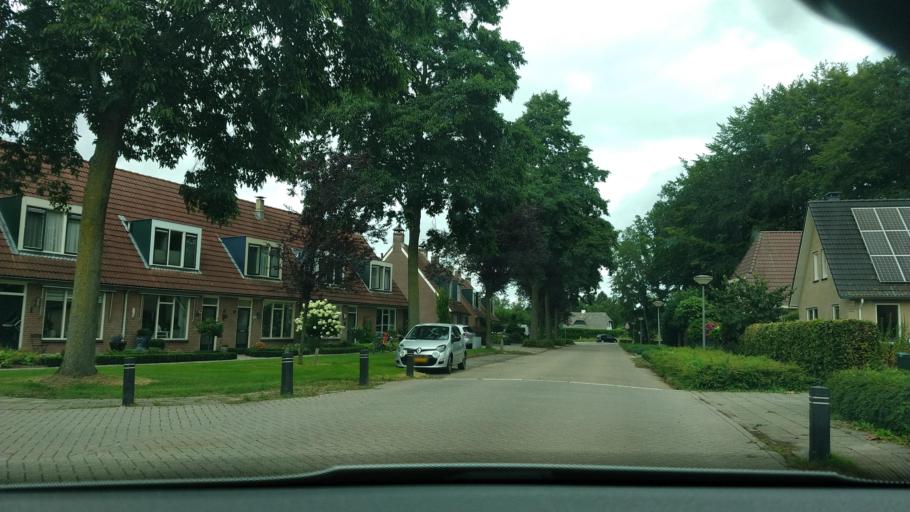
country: NL
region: Gelderland
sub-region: Gemeente Ermelo
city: Ermelo
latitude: 52.3007
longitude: 5.6014
